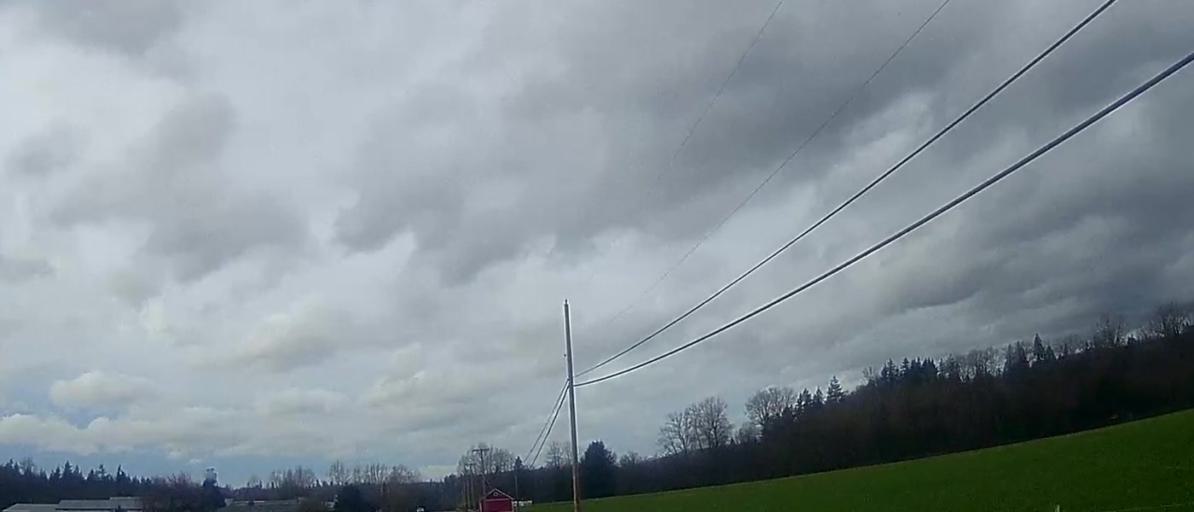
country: US
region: Washington
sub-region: Skagit County
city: Sedro-Woolley
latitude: 48.5835
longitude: -122.2653
